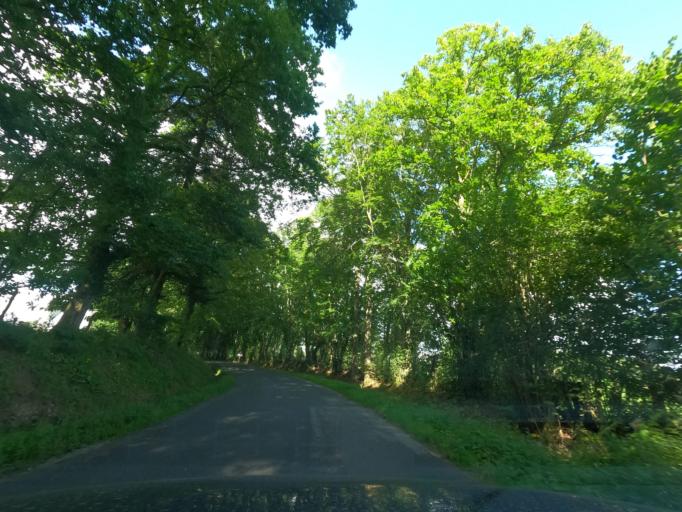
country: FR
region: Lower Normandy
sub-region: Departement de l'Orne
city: Gace
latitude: 48.7819
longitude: 0.2594
